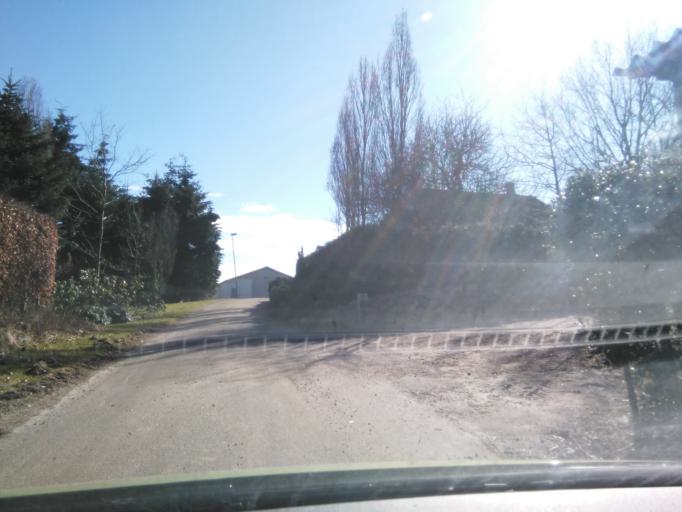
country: DK
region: Central Jutland
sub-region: Skanderborg Kommune
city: Stilling
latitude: 55.9710
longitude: 10.0104
